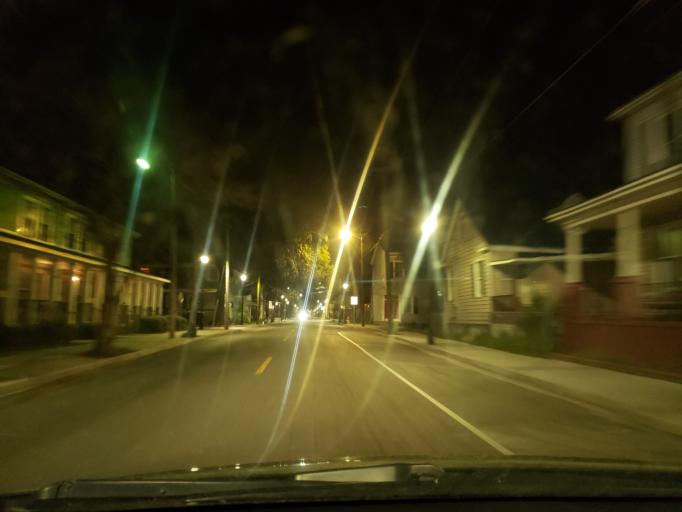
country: US
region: Georgia
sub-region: Chatham County
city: Savannah
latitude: 32.0626
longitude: -81.0802
